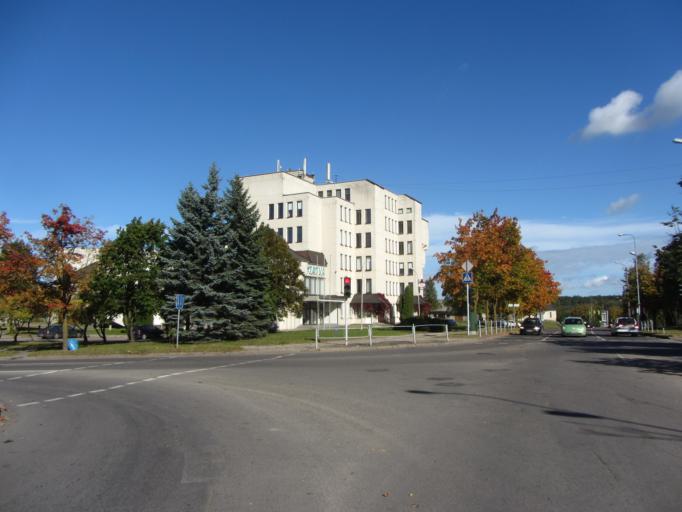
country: LT
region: Utenos apskritis
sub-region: Utena
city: Utena
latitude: 55.5094
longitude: 25.5983
